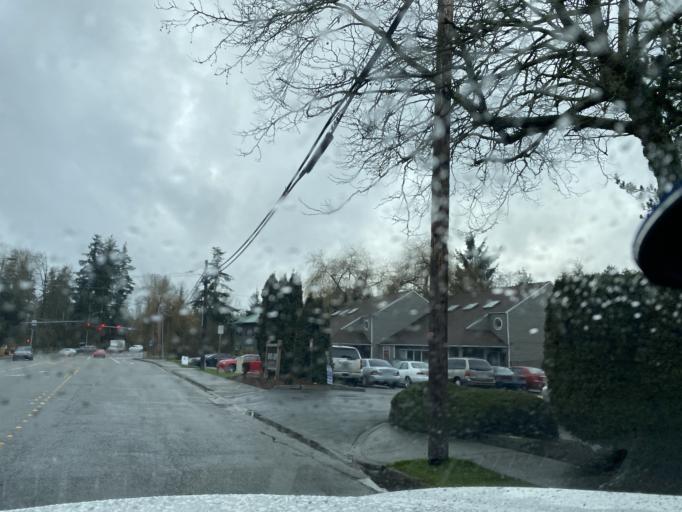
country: US
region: Washington
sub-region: Snohomish County
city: Lynnwood
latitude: 47.8186
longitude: -122.3006
